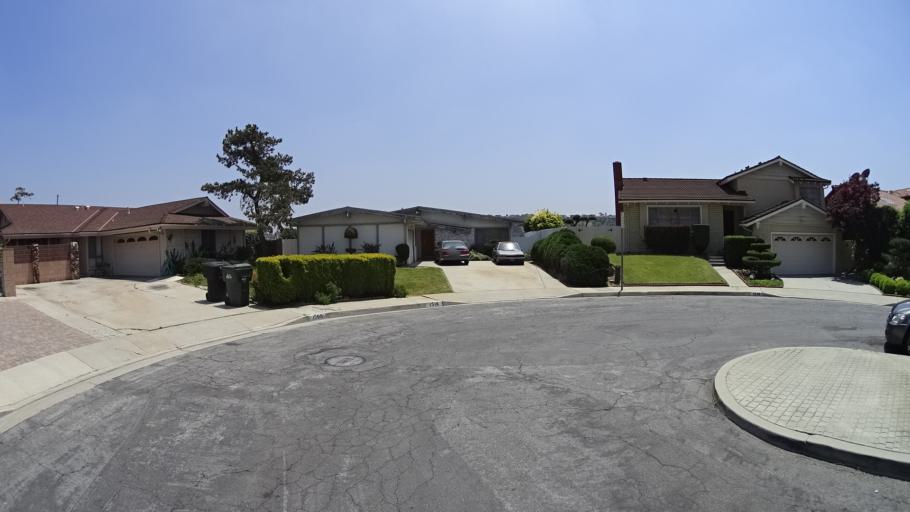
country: US
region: California
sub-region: Los Angeles County
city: Belvedere
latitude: 34.0570
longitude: -118.1500
